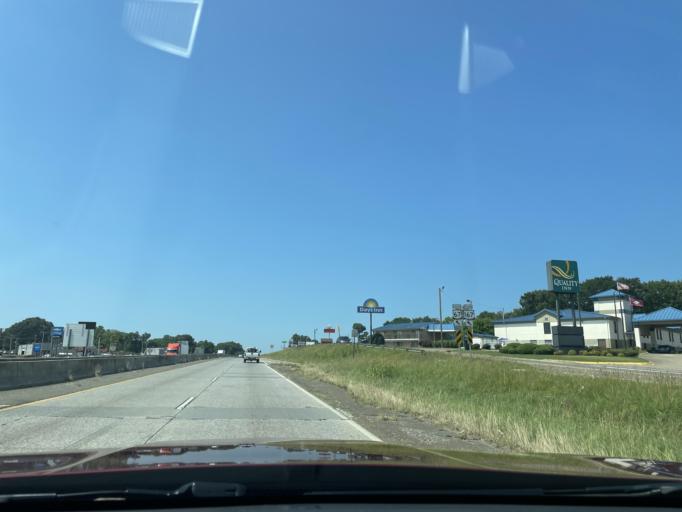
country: US
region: Arkansas
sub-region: Pulaski County
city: Jacksonville
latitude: 34.8807
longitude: -92.1129
